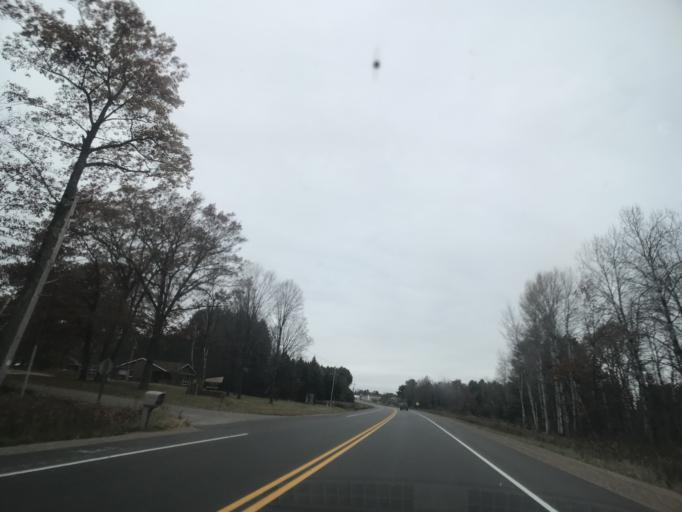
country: US
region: Wisconsin
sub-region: Menominee County
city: Legend Lake
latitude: 45.2945
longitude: -88.5131
